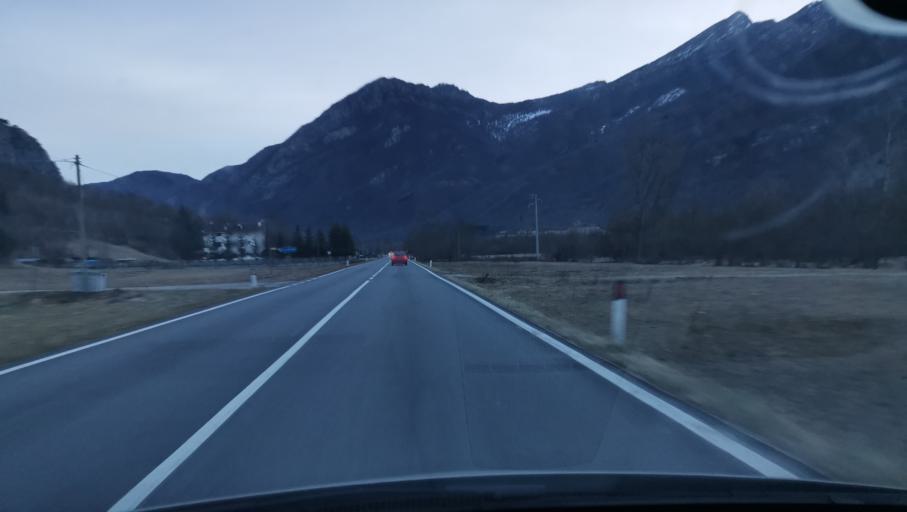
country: IT
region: Piedmont
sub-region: Provincia di Cuneo
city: Valloriate
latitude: 44.3108
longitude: 7.3617
